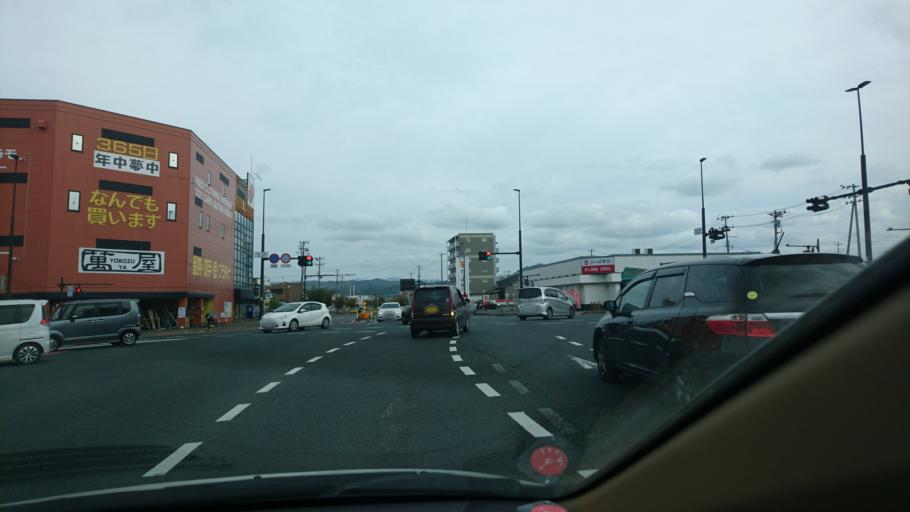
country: JP
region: Iwate
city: Morioka-shi
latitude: 39.6850
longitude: 141.1353
